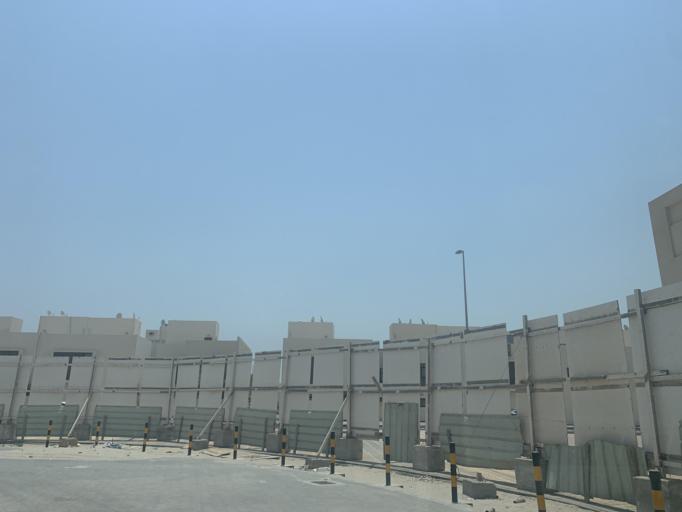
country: BH
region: Muharraq
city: Al Hadd
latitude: 26.2358
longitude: 50.6682
